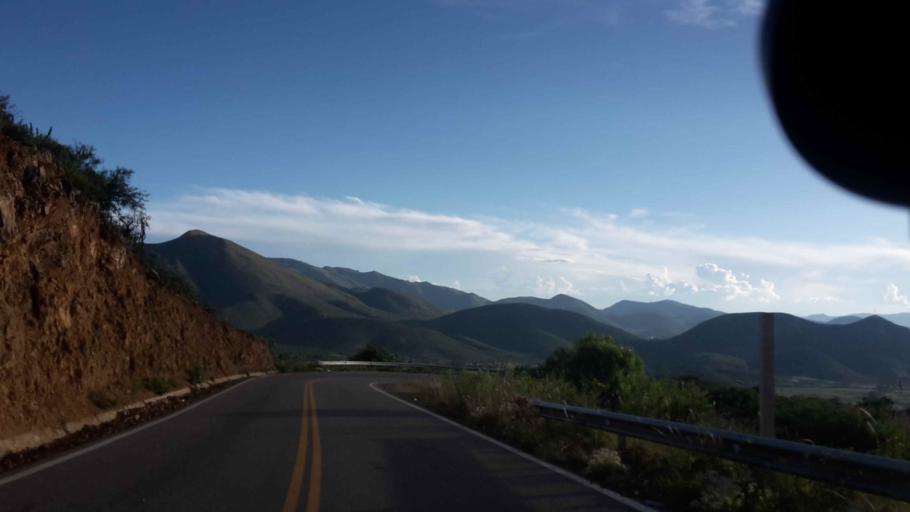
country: BO
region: Cochabamba
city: Arani
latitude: -17.5884
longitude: -65.7536
